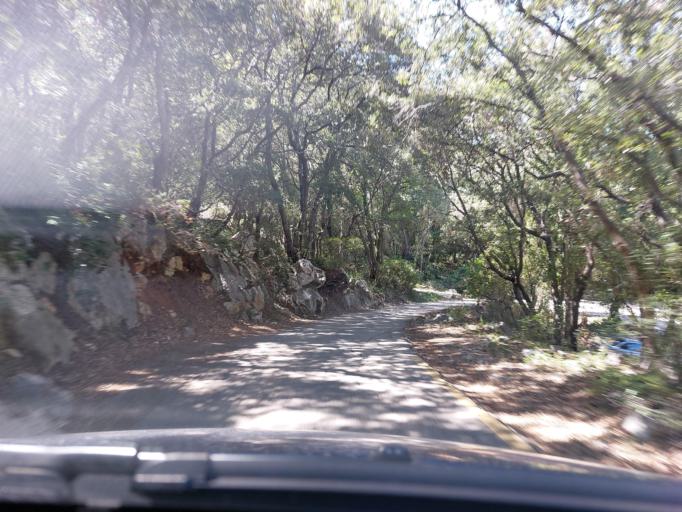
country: HR
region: Dubrovacko-Neretvanska
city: Smokvica
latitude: 42.7700
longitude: 16.8975
